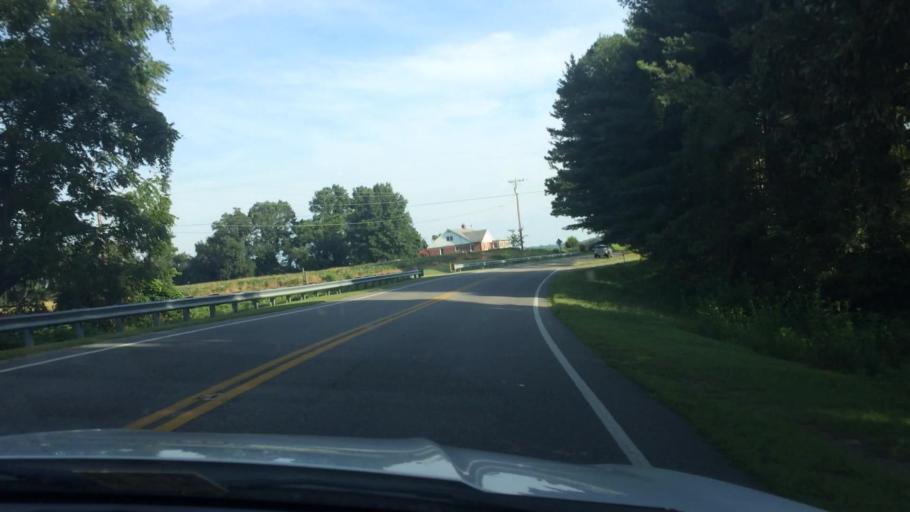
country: US
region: Virginia
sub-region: Middlesex County
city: Deltaville
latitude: 37.5054
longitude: -76.4194
